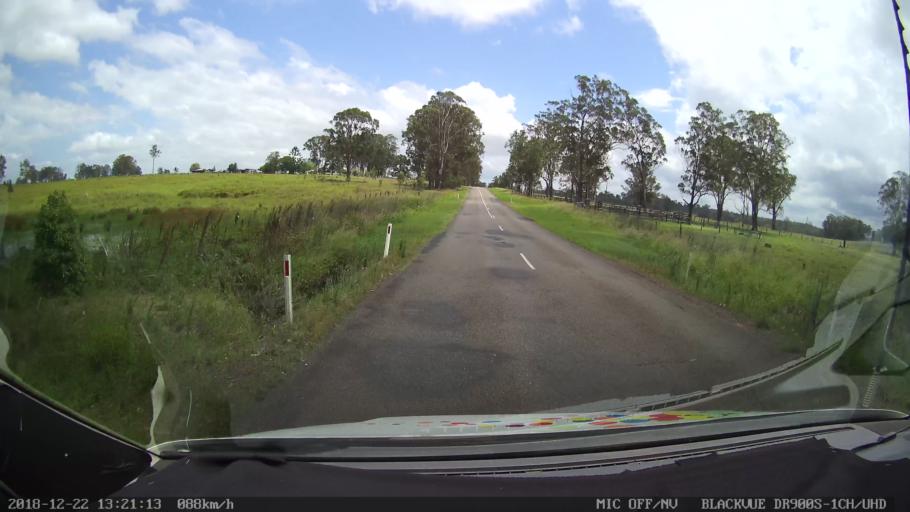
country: AU
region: New South Wales
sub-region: Clarence Valley
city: Coutts Crossing
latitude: -29.7747
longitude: 152.9223
